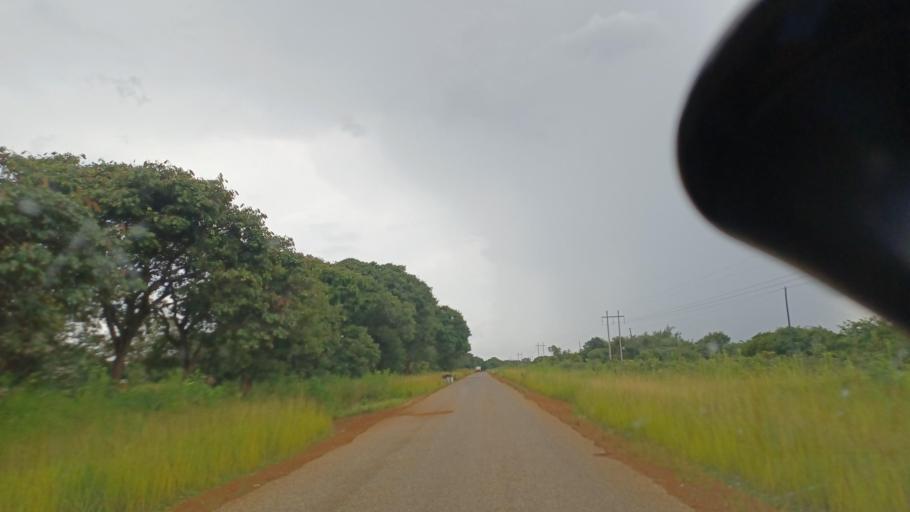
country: ZM
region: North-Western
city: Kasempa
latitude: -13.0409
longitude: 25.9933
